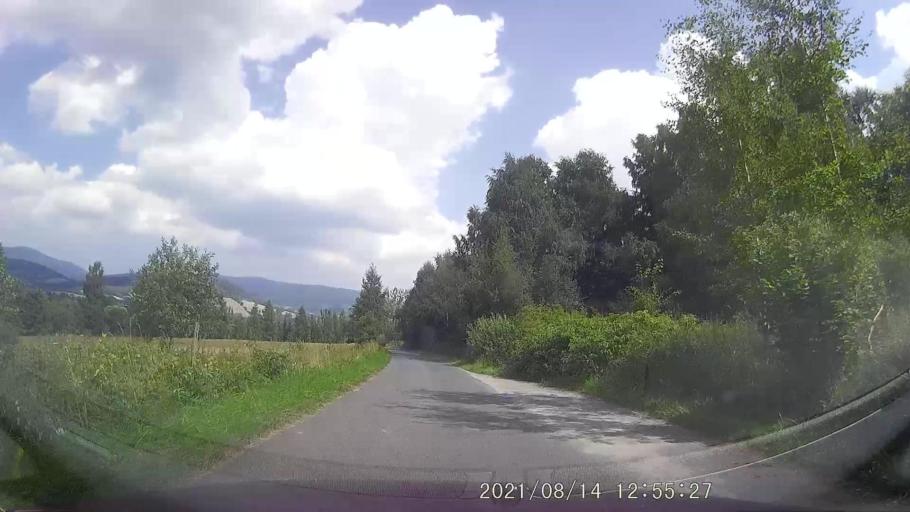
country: PL
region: Lower Silesian Voivodeship
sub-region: Powiat klodzki
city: Ladek-Zdroj
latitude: 50.3316
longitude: 16.8308
